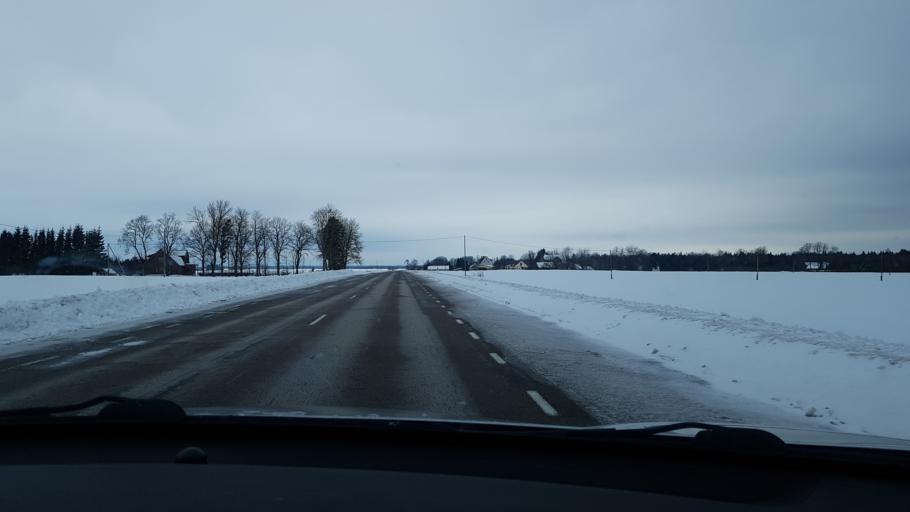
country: EE
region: Jaervamaa
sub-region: Jaerva-Jaani vald
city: Jarva-Jaani
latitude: 58.9113
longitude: 25.8516
